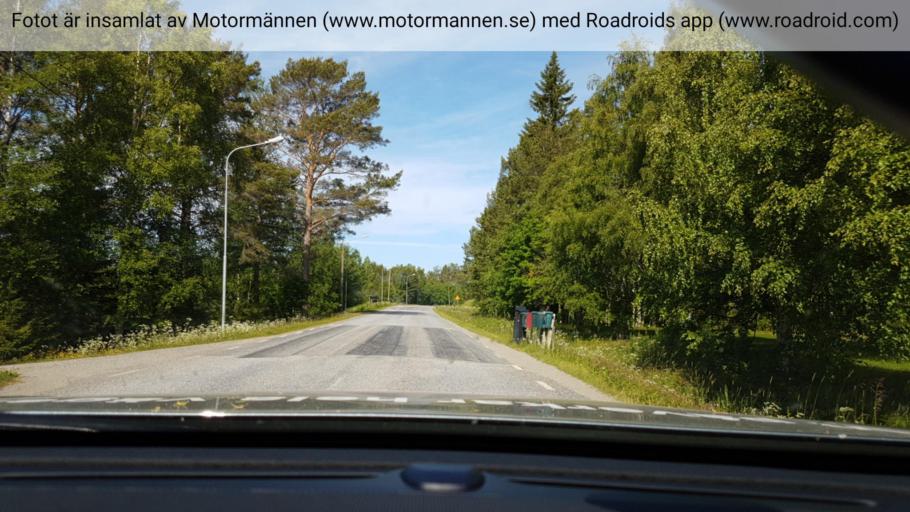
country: SE
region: Vaesterbotten
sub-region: Dorotea Kommun
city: Dorotea
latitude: 64.3399
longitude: 16.2670
